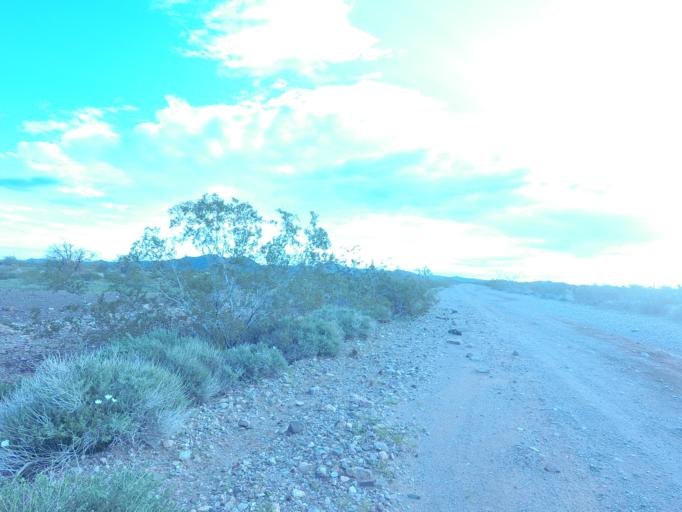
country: US
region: Arizona
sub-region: La Paz County
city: Quartzsite
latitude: 33.5332
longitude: -114.1932
